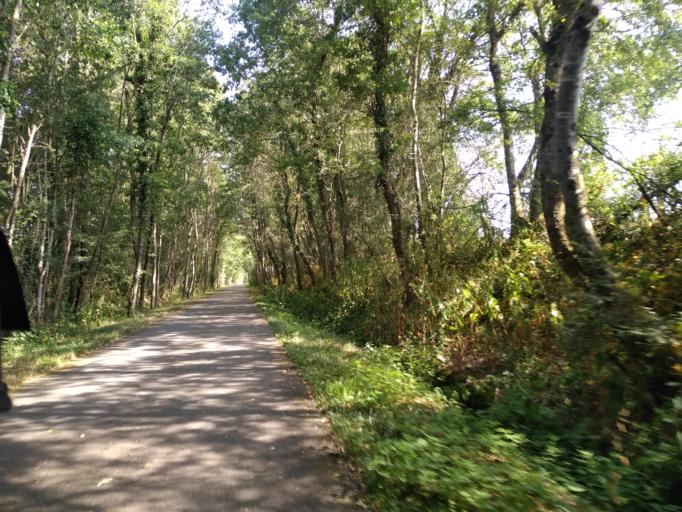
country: FR
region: Bourgogne
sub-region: Departement de Saone-et-Loire
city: Marcigny
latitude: 46.3064
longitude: 4.0289
